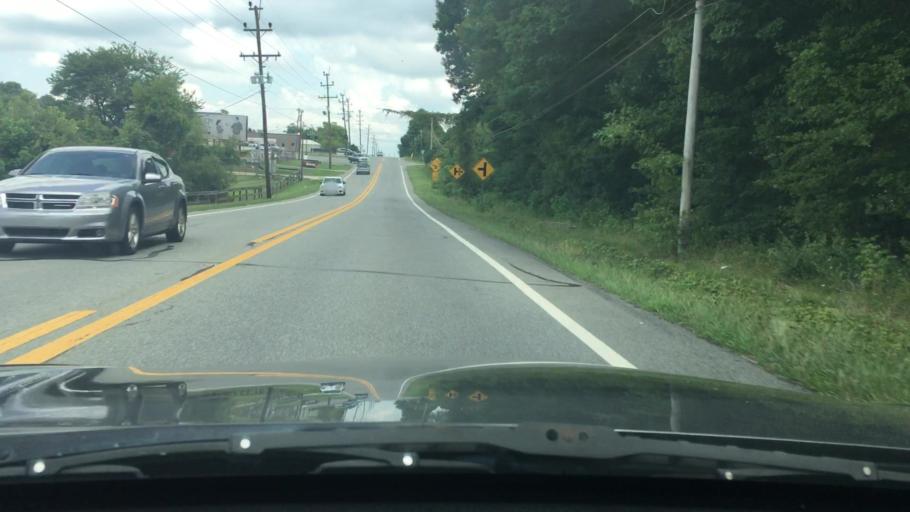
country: US
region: North Carolina
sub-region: Alamance County
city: Mebane
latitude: 36.0985
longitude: -79.2853
